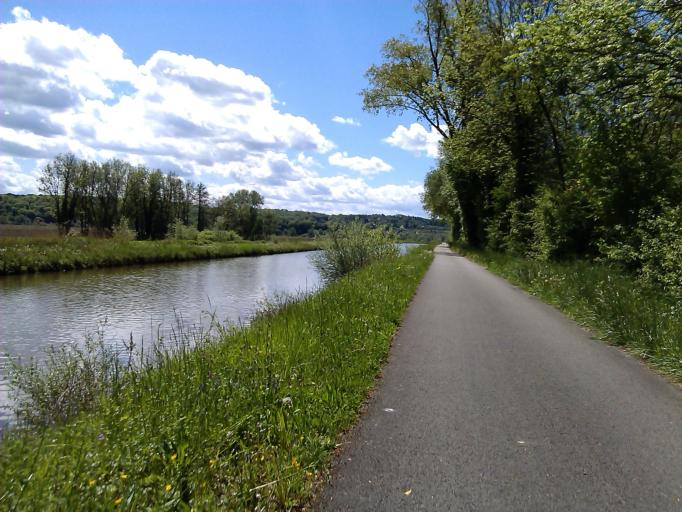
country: FR
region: Franche-Comte
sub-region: Territoire de Belfort
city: Mezire
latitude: 47.5373
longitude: 6.9096
